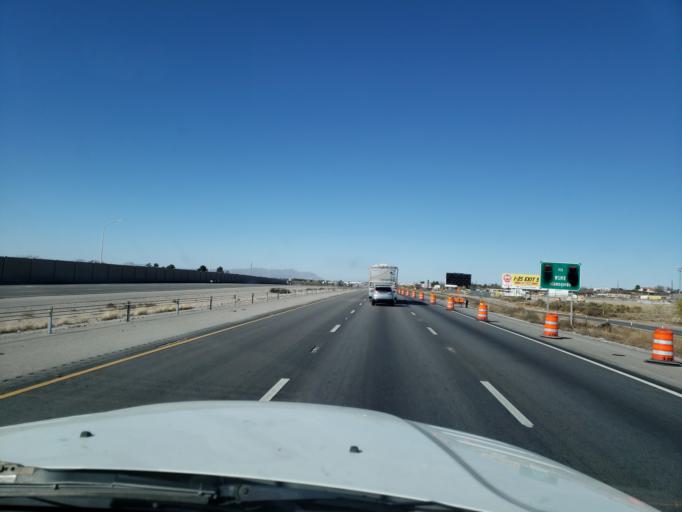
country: US
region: New Mexico
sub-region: Dona Ana County
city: University Park
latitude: 32.2467
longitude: -106.7219
